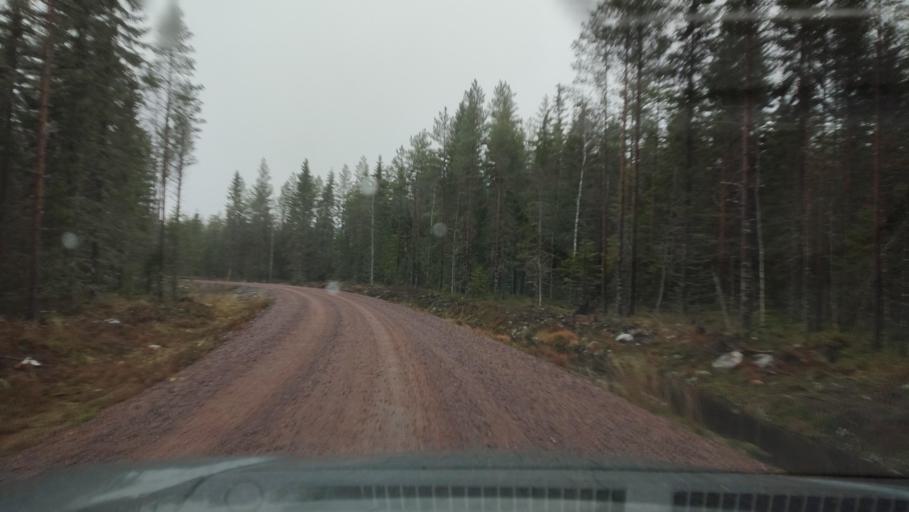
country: FI
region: Southern Ostrobothnia
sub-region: Suupohja
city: Karijoki
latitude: 62.1798
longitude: 21.7297
